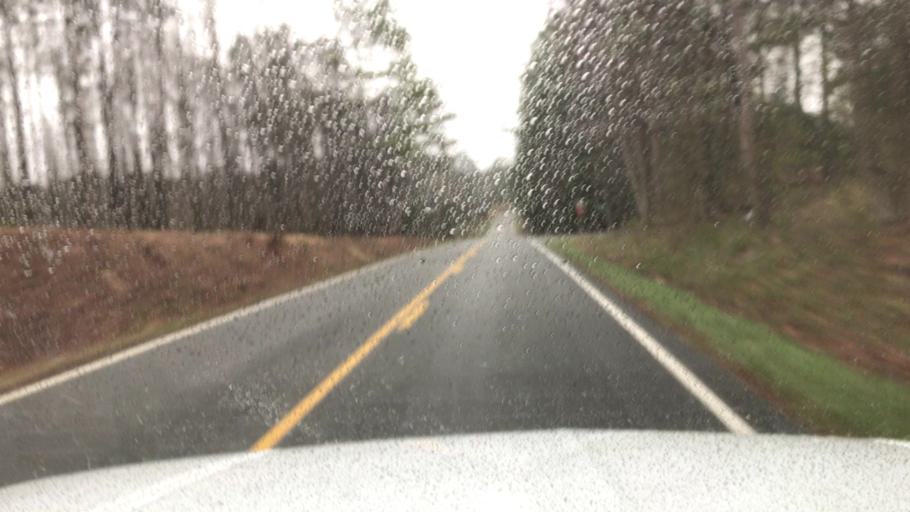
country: US
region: Virginia
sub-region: Henrico County
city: Short Pump
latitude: 37.6553
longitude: -77.6781
